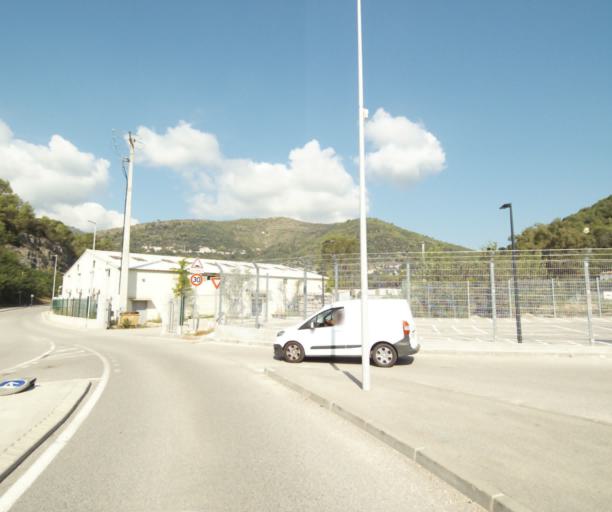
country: FR
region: Provence-Alpes-Cote d'Azur
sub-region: Departement des Alpes-Maritimes
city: Drap
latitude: 43.7644
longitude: 7.3366
